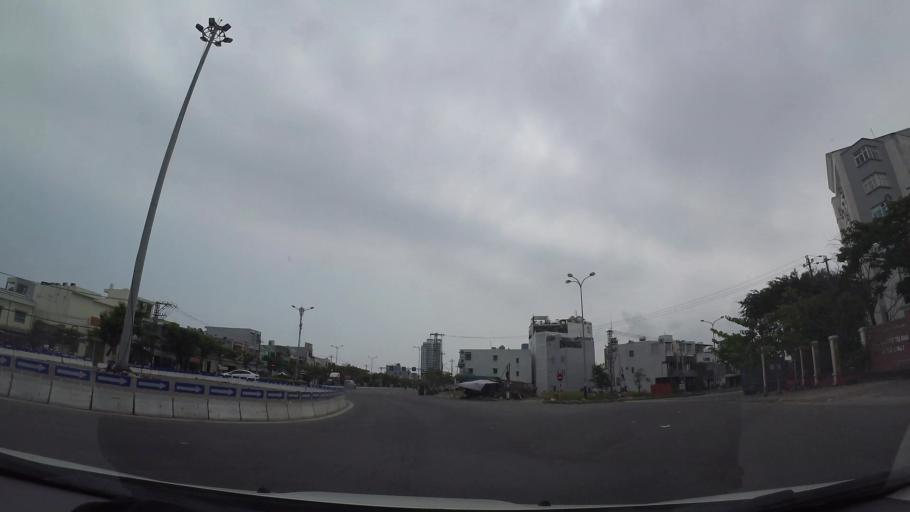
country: VN
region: Da Nang
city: Da Nang
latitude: 16.1019
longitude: 108.2474
